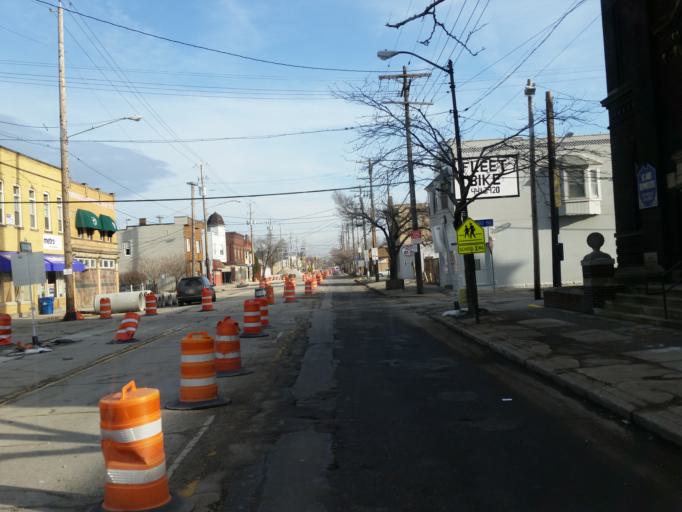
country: US
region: Ohio
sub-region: Cuyahoga County
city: Newburgh Heights
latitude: 41.4558
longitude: -81.6559
